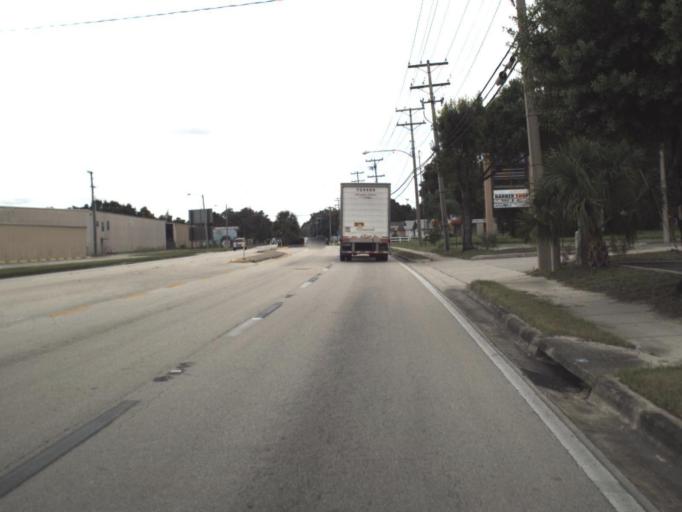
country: US
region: Florida
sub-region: Polk County
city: Bartow
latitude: 27.8817
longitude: -81.8286
